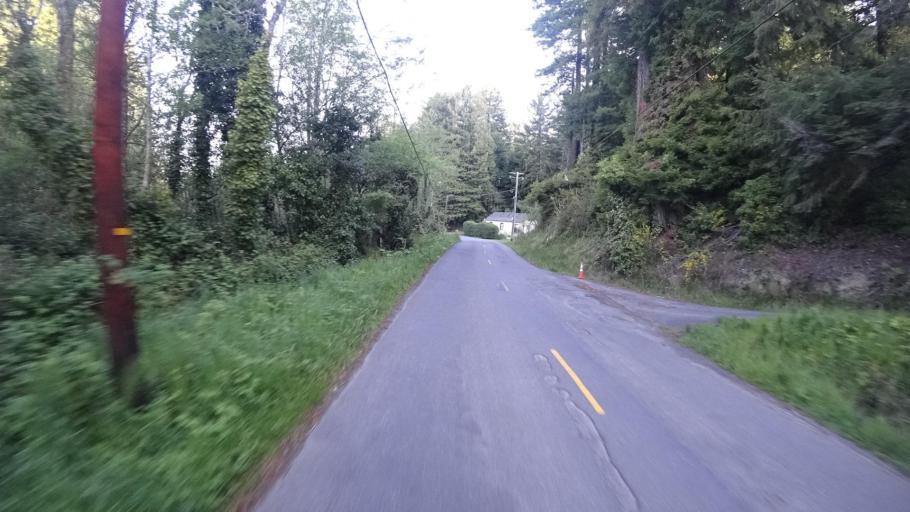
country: US
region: California
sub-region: Humboldt County
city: Myrtletown
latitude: 40.7758
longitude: -124.1131
